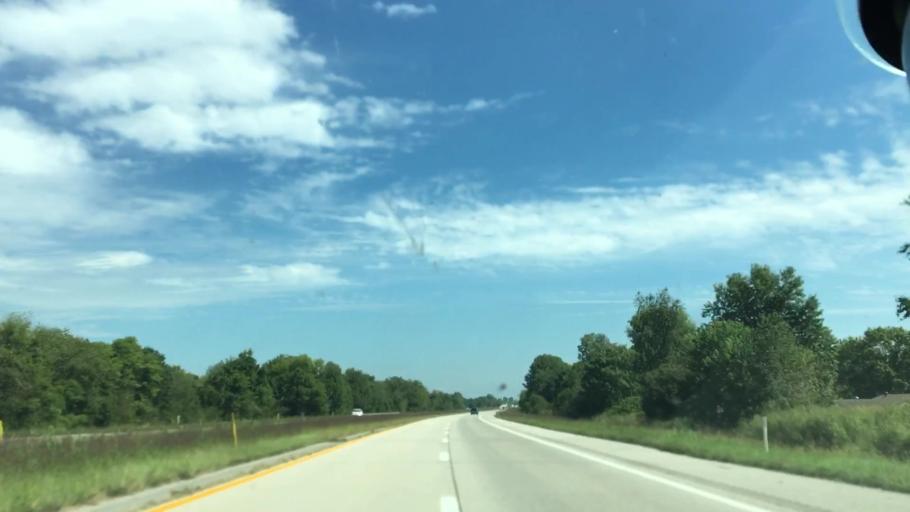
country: US
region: Kentucky
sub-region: Daviess County
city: Owensboro
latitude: 37.7683
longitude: -87.1977
